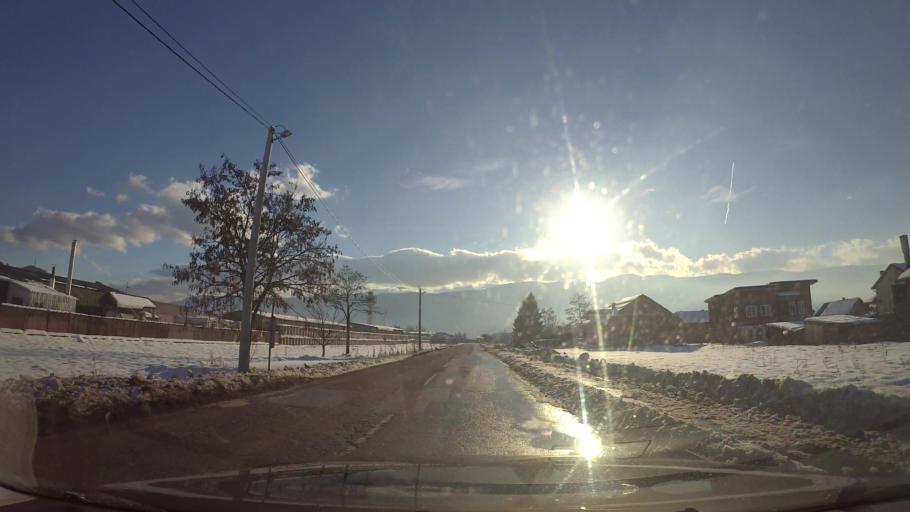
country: BA
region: Federation of Bosnia and Herzegovina
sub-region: Kanton Sarajevo
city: Sarajevo
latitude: 43.8161
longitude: 18.3416
